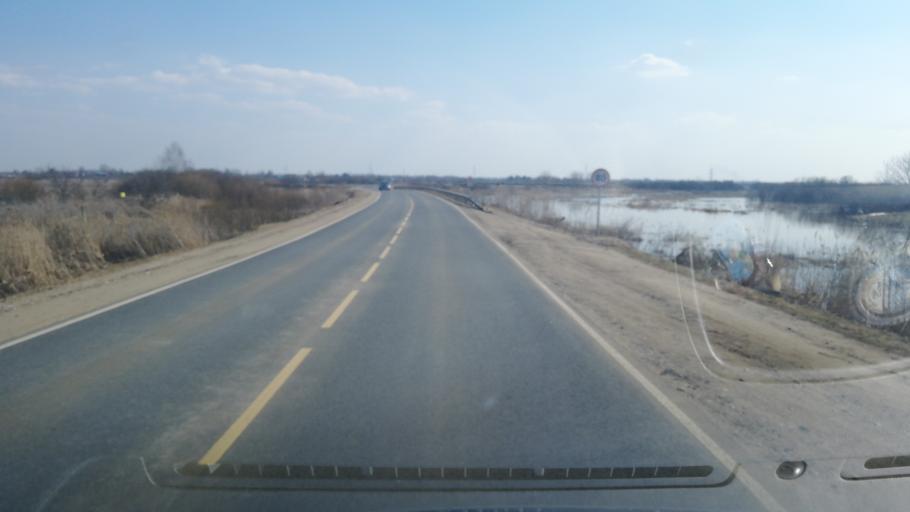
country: RU
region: Jaroslavl
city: Semibratovo
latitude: 57.2334
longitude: 39.5056
